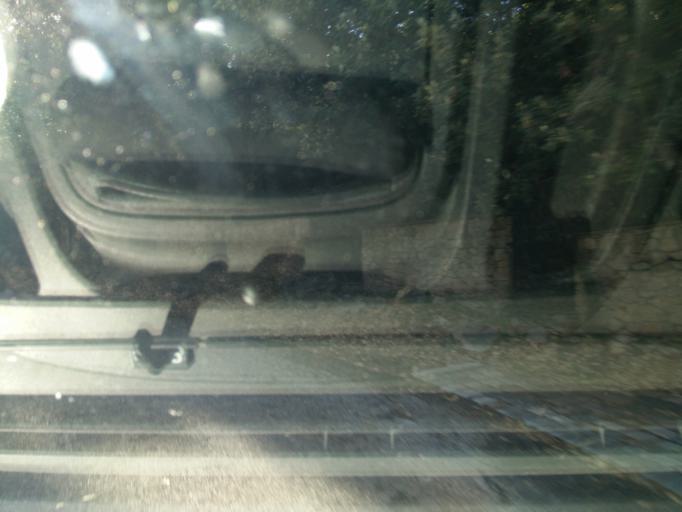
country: FR
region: Provence-Alpes-Cote d'Azur
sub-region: Departement du Var
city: Belgentier
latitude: 43.2187
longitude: 5.9780
